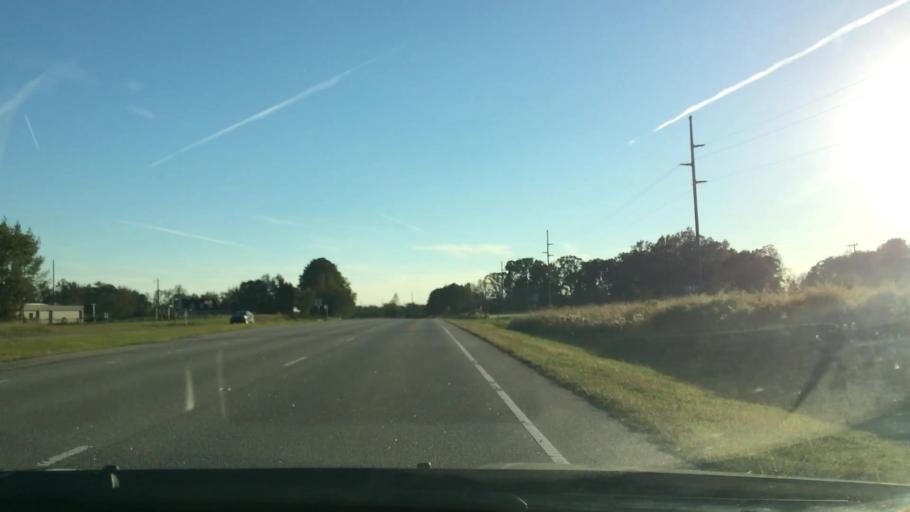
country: US
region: North Carolina
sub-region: Pitt County
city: Grifton
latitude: 35.3974
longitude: -77.4419
